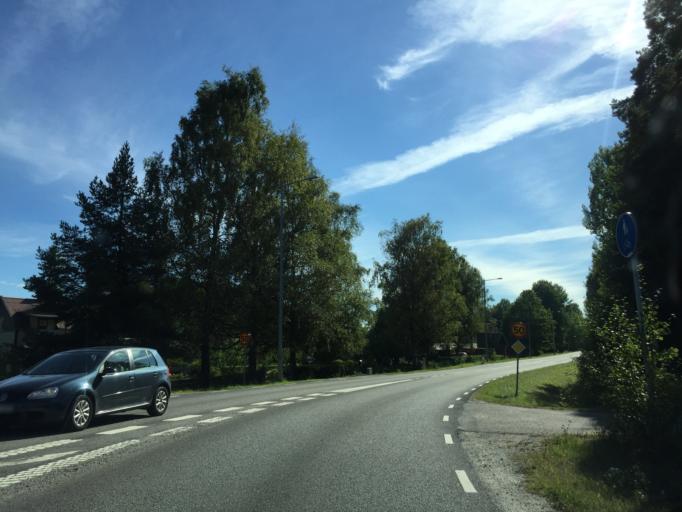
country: SE
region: OErebro
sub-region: Orebro Kommun
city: Orebro
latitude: 59.2983
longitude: 15.2526
